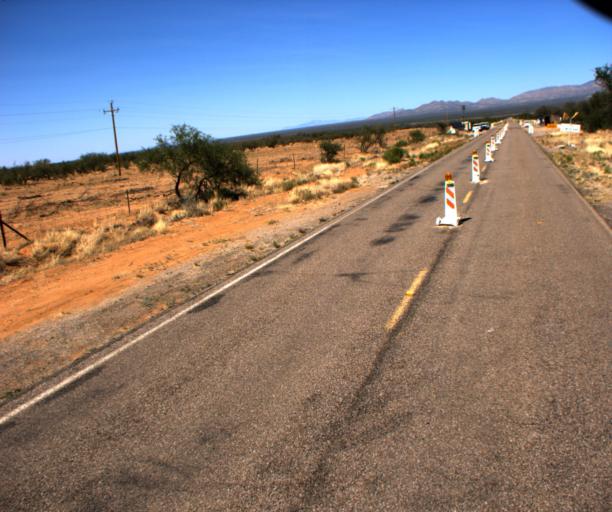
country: US
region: Arizona
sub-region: Pima County
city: Three Points
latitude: 31.8276
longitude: -111.4262
